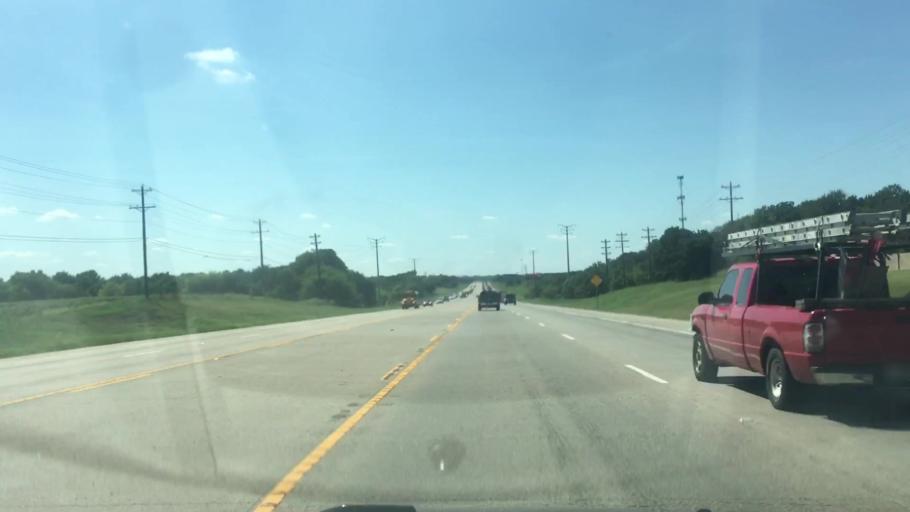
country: US
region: Texas
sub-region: Denton County
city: Little Elm
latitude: 33.2221
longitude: -96.9404
